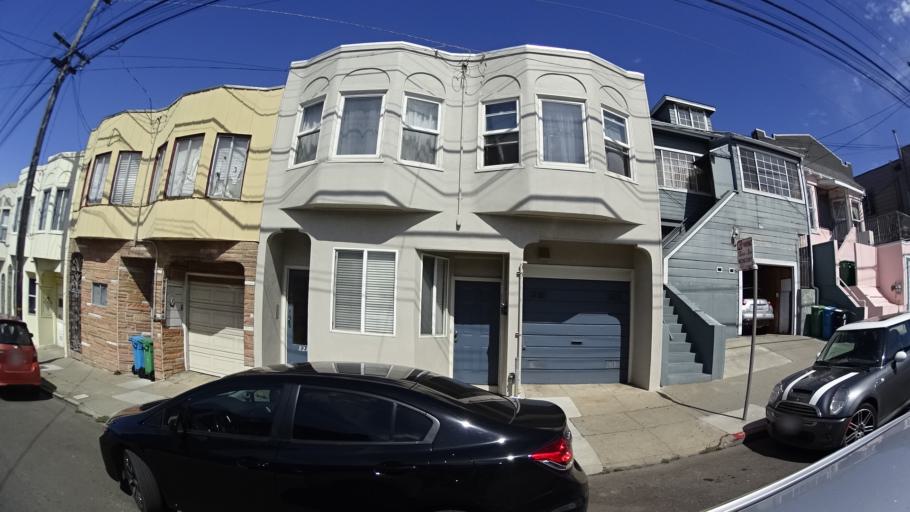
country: US
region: California
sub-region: San Mateo County
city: Daly City
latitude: 37.7183
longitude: -122.4303
